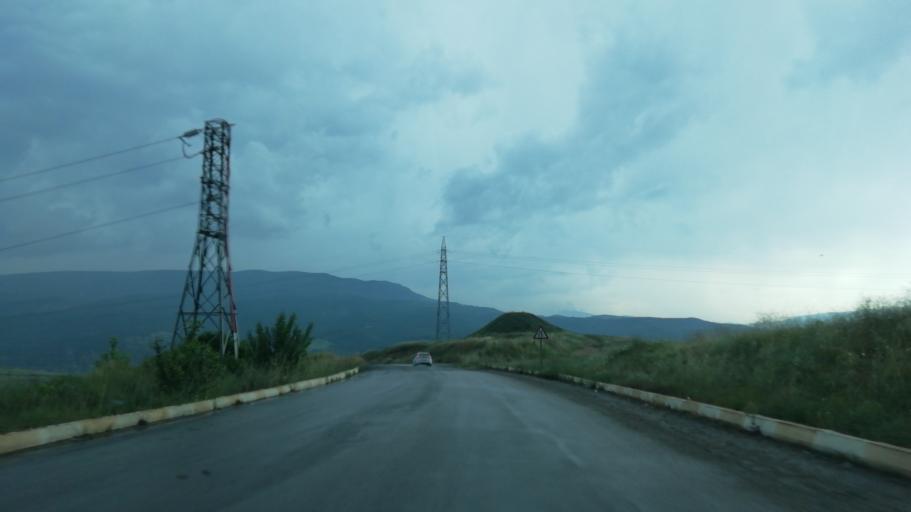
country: TR
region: Karabuk
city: Safranbolu
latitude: 41.2365
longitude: 32.6828
